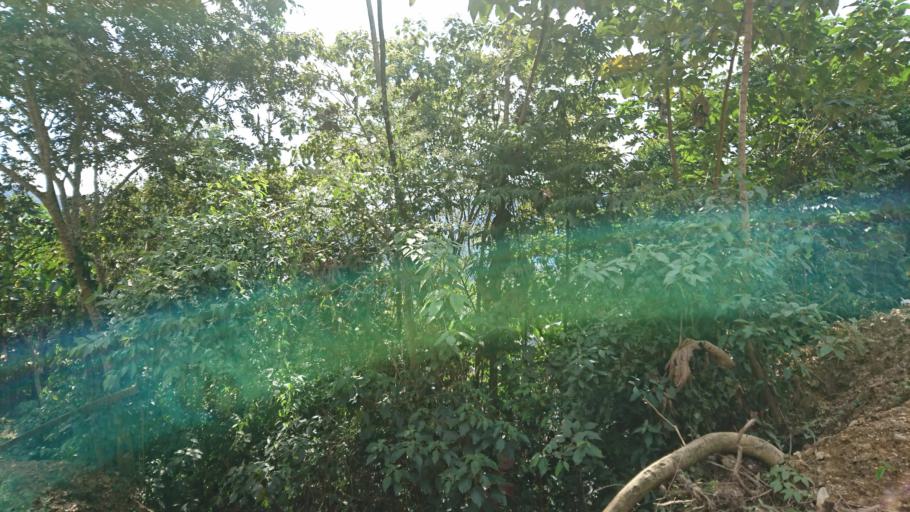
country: BO
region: La Paz
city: Coroico
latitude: -16.0884
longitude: -67.7850
